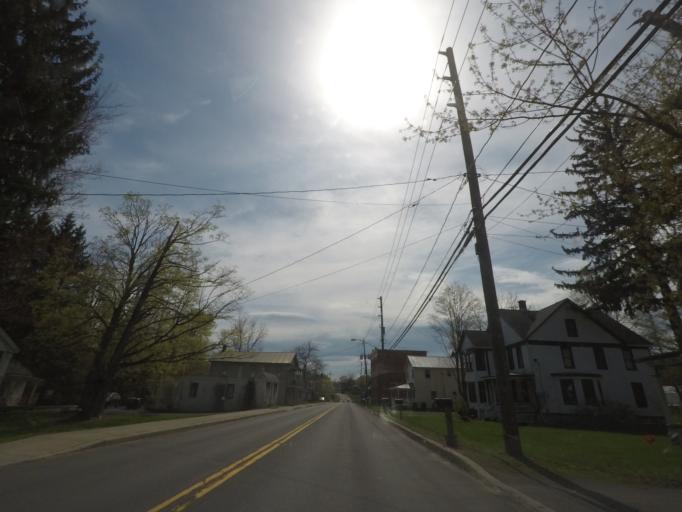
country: US
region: New York
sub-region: Columbia County
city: Chatham
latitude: 42.3278
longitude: -73.6174
